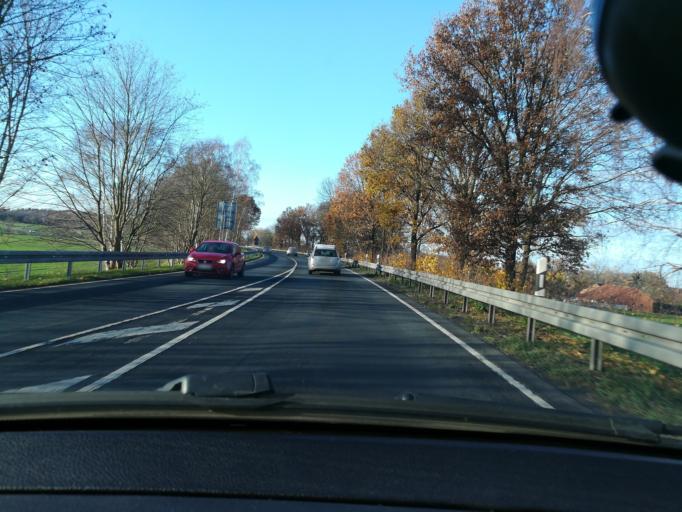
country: DE
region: Lower Saxony
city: Kirchdorf
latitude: 52.5915
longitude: 8.8363
